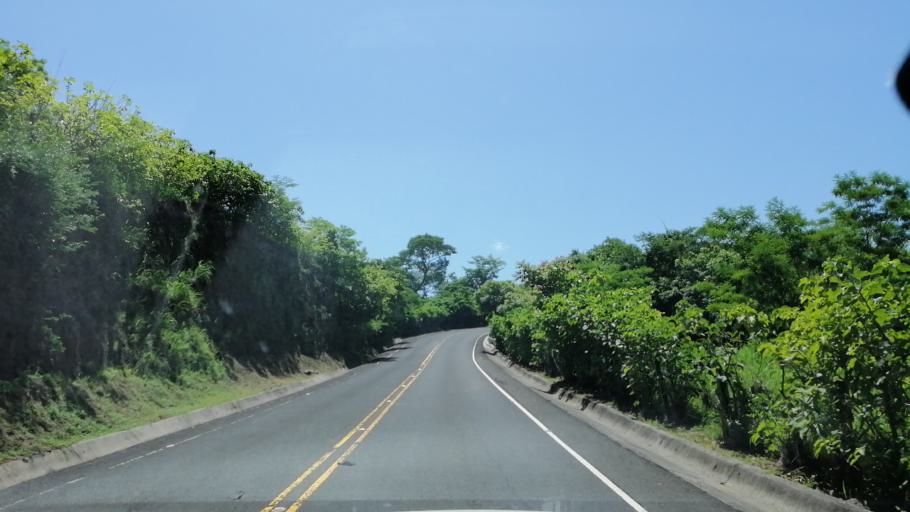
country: SV
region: San Miguel
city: Sesori
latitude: 13.8070
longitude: -88.3924
